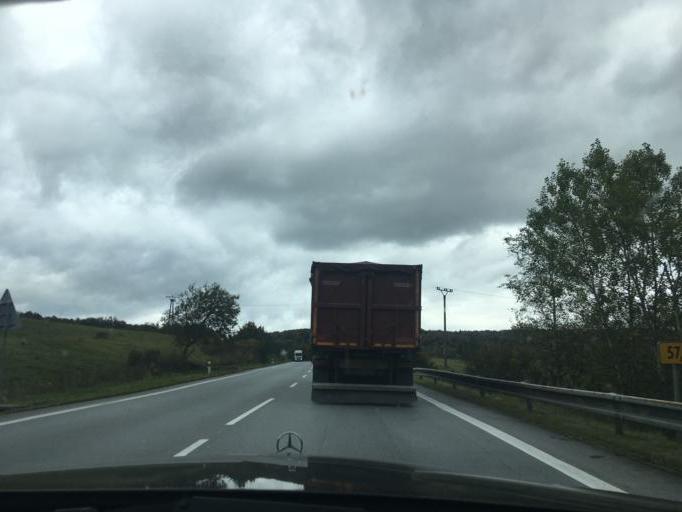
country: PL
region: Subcarpathian Voivodeship
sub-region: Powiat krosnienski
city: Jasliska
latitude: 49.3979
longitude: 21.7015
